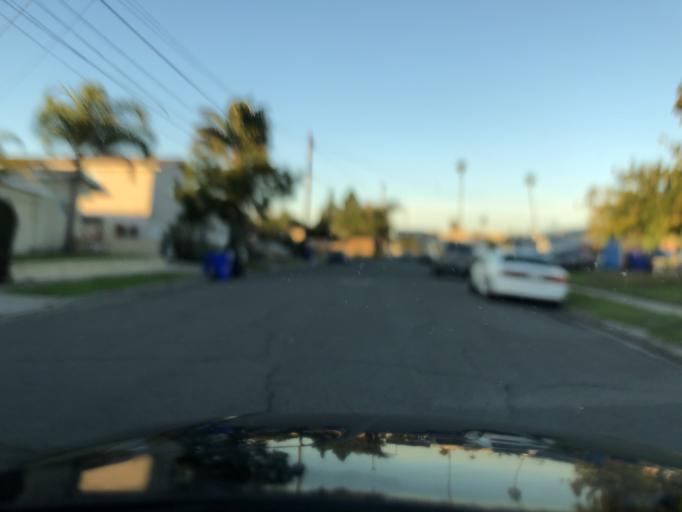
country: US
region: California
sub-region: San Diego County
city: La Jolla
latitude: 32.8328
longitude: -117.1811
